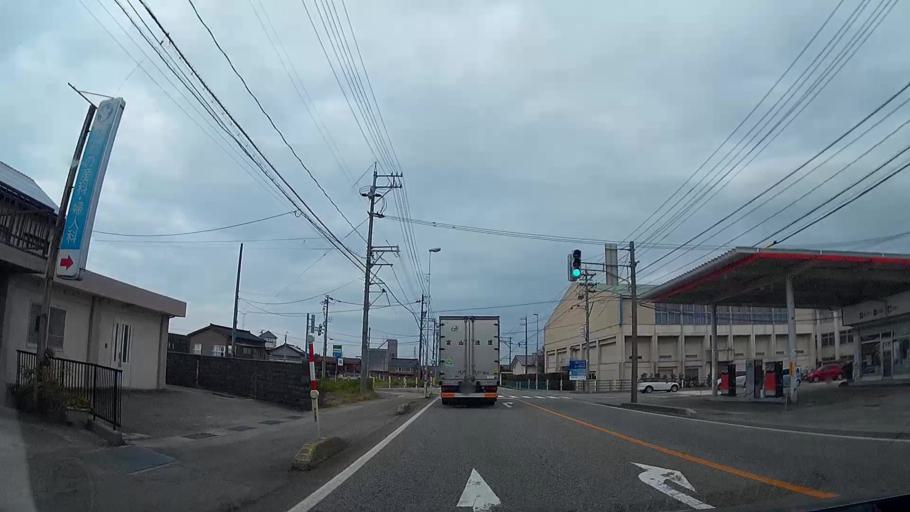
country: JP
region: Toyama
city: Nyuzen
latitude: 36.9339
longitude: 137.5038
